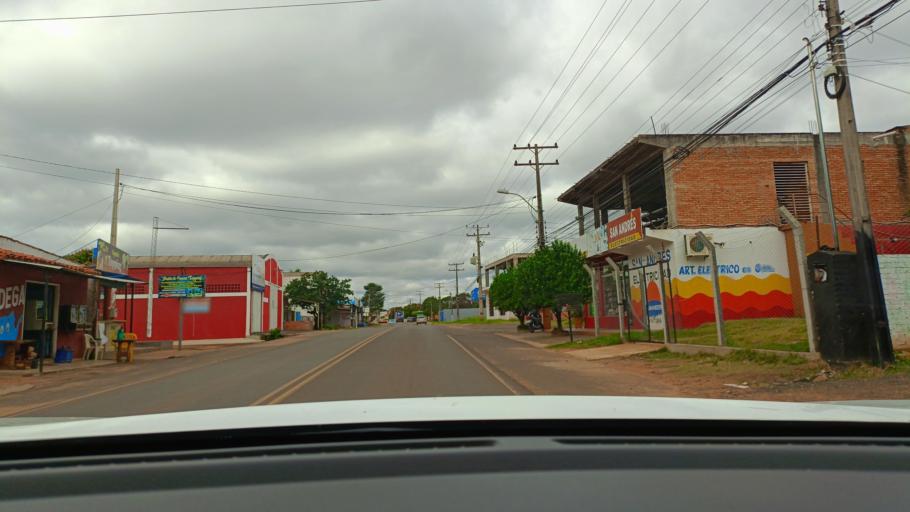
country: PY
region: San Pedro
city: Guayaybi
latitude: -24.6706
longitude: -56.4541
